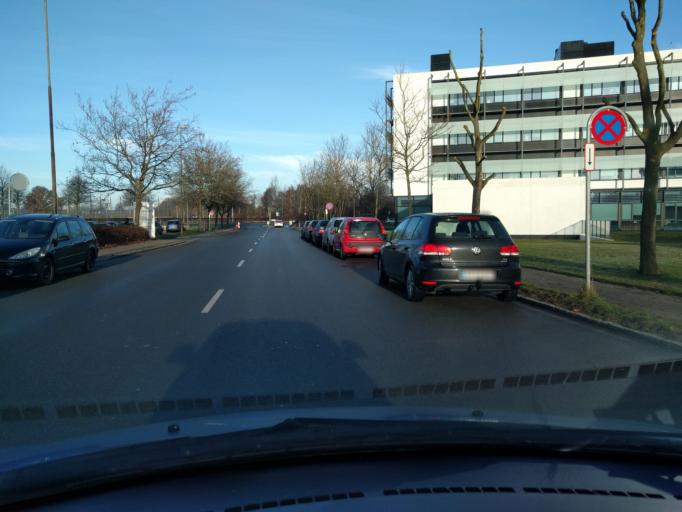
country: DK
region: South Denmark
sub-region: Odense Kommune
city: Odense
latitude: 55.3876
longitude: 10.3613
